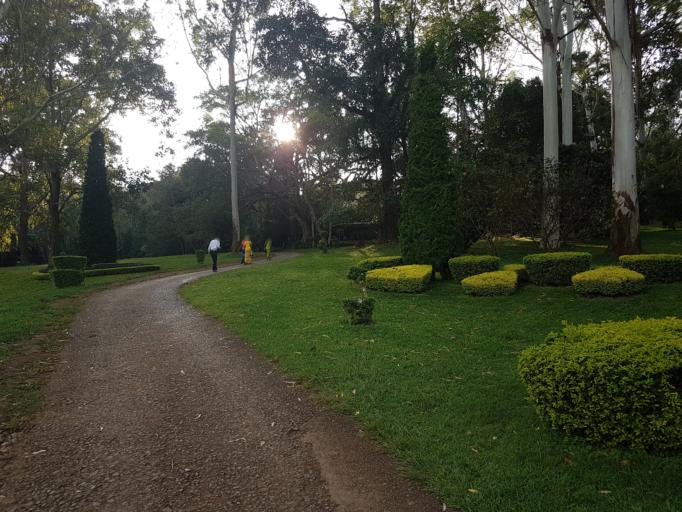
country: MM
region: Mandalay
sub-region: Pyin Oo Lwin District
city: Pyin Oo Lwin
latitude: 21.9939
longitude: 96.4692
